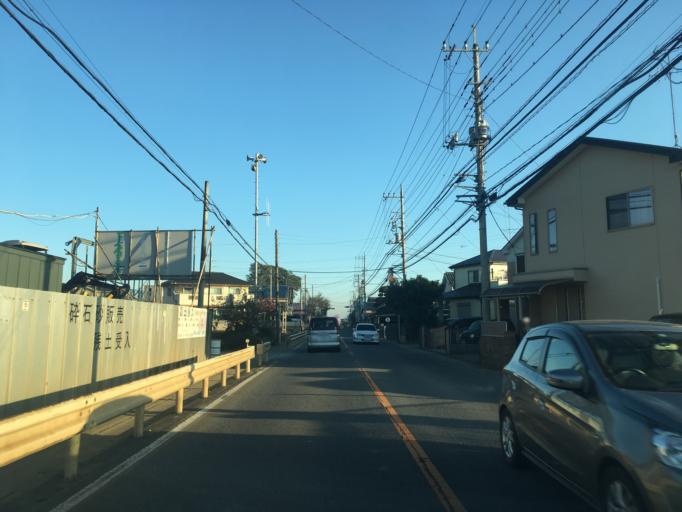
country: JP
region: Saitama
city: Kamifukuoka
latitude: 35.8616
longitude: 139.4705
